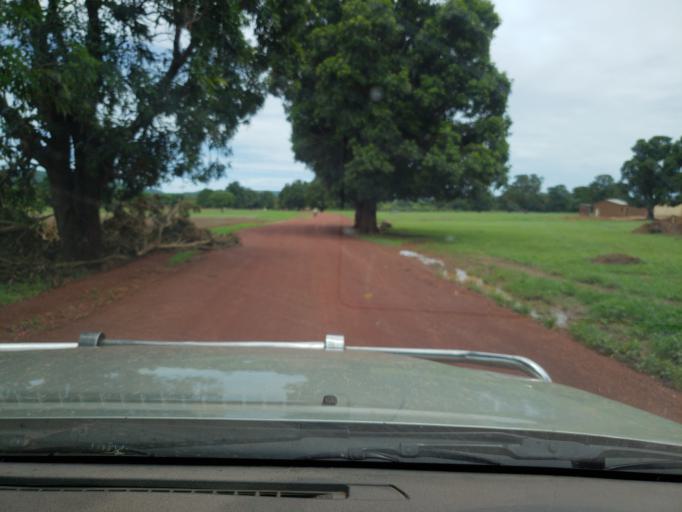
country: ML
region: Sikasso
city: Sikasso
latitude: 11.6719
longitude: -6.3392
